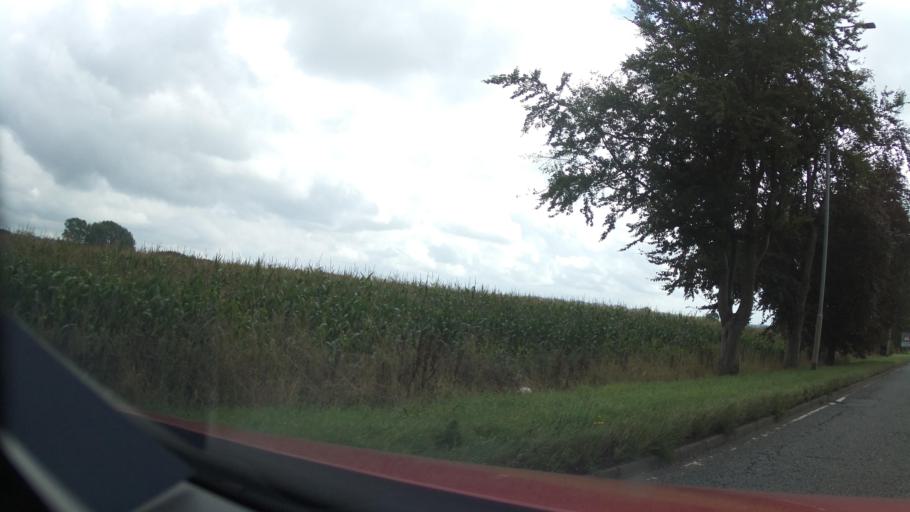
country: GB
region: England
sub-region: Staffordshire
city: Barlaston
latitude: 52.9577
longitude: -2.1938
